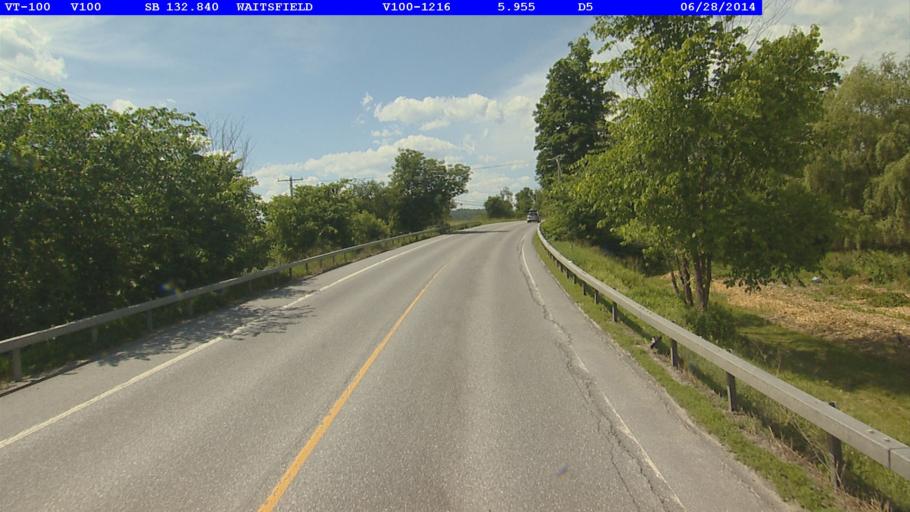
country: US
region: Vermont
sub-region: Washington County
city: Waterbury
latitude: 44.2140
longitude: -72.7932
